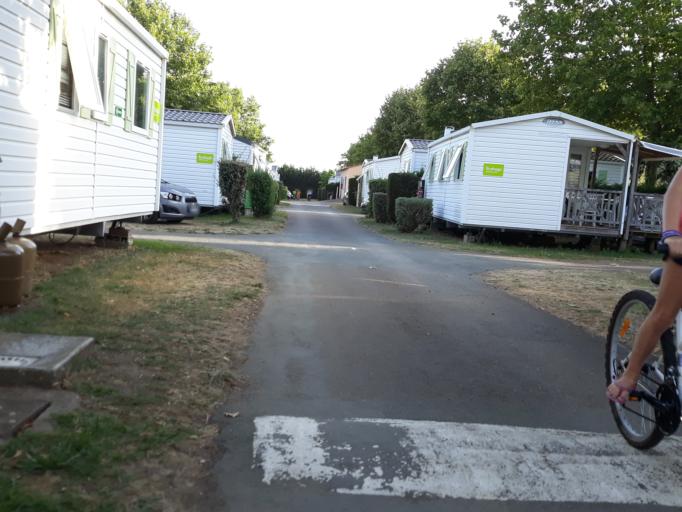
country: FR
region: Poitou-Charentes
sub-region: Departement de la Charente-Maritime
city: Saint-Laurent-de-la-Pree
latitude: 45.9876
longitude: -1.0528
